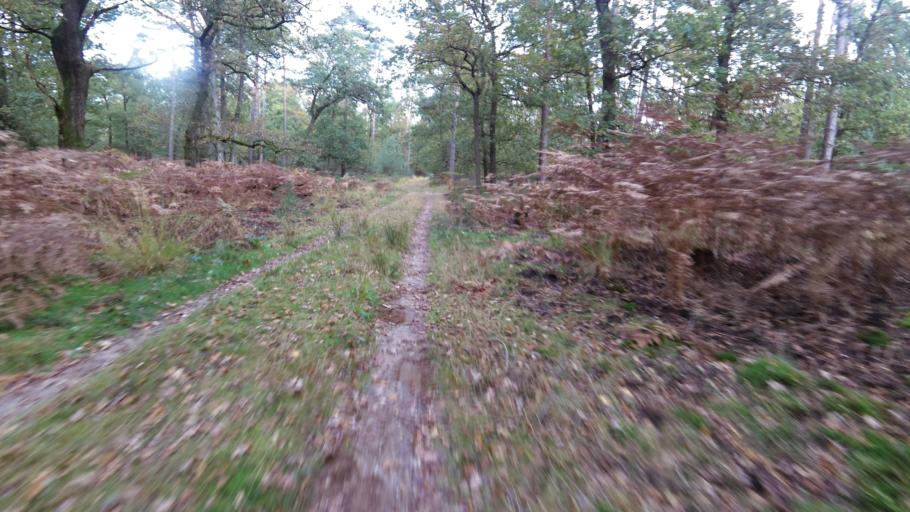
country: NL
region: Gelderland
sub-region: Gemeente Epe
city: Vaassen
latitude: 52.3201
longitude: 5.8810
